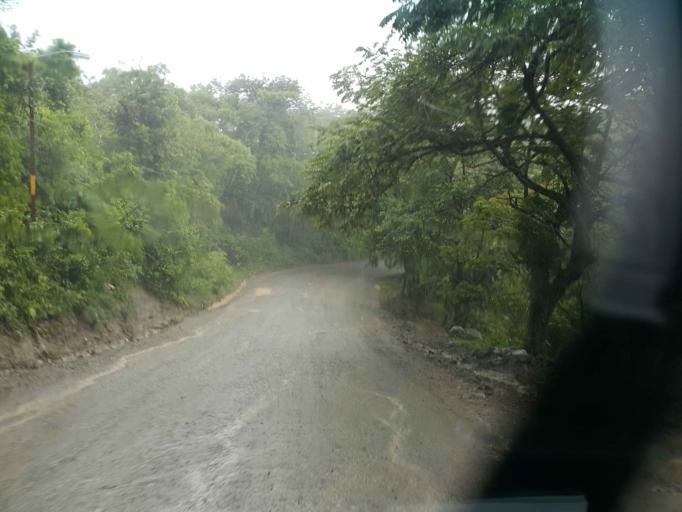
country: CR
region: Guanacaste
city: Juntas
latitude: 10.2442
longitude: -84.8459
